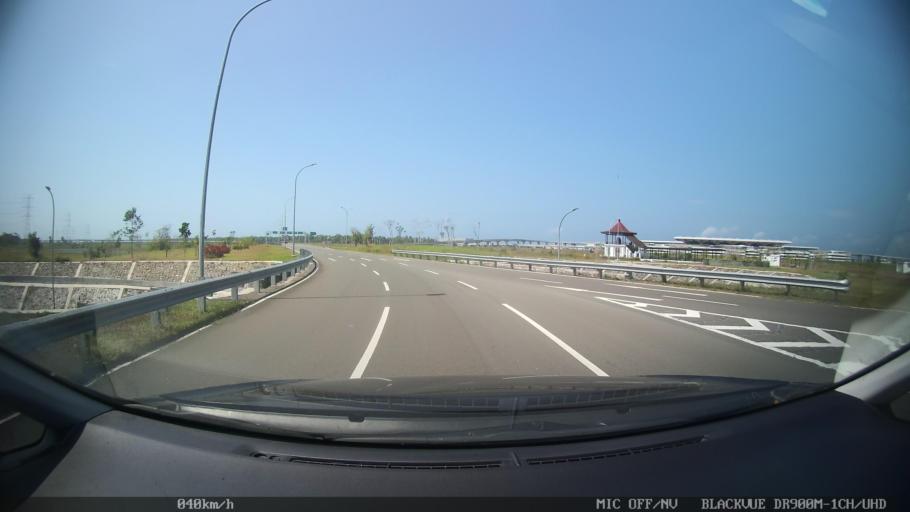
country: ID
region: Daerah Istimewa Yogyakarta
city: Srandakan
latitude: -7.8917
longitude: 110.0623
